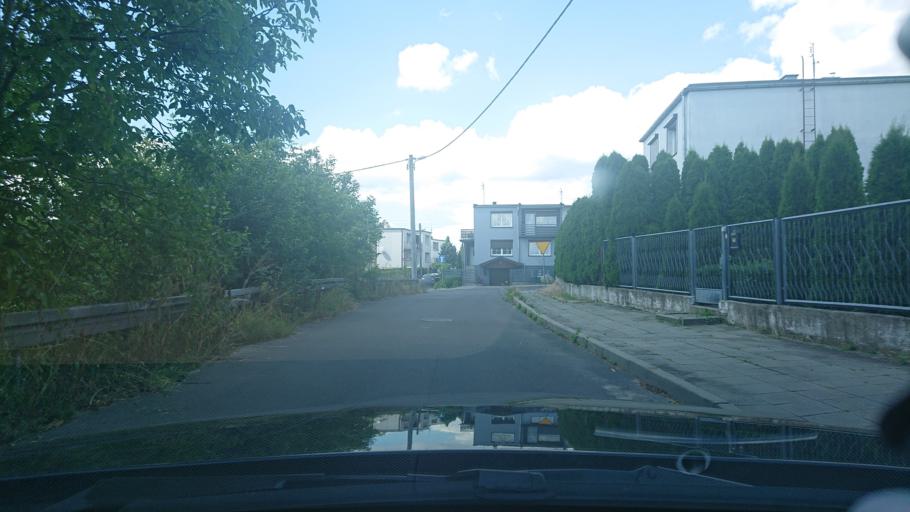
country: PL
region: Greater Poland Voivodeship
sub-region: Powiat gnieznienski
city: Gniezno
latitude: 52.5354
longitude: 17.6336
